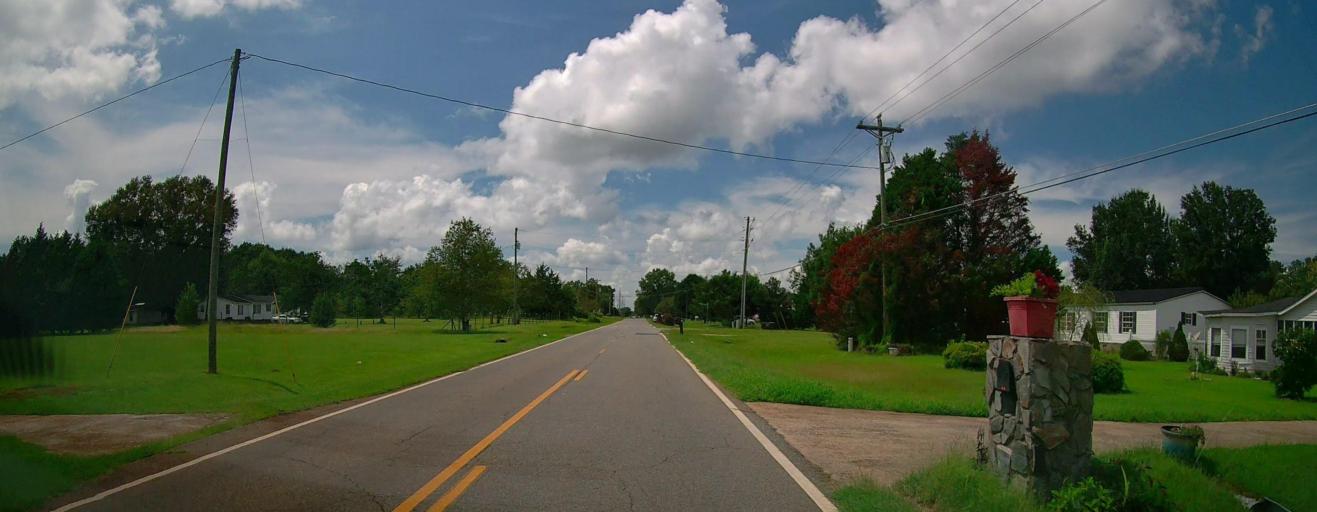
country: US
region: Georgia
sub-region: Houston County
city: Perry
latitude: 32.5106
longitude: -83.7312
